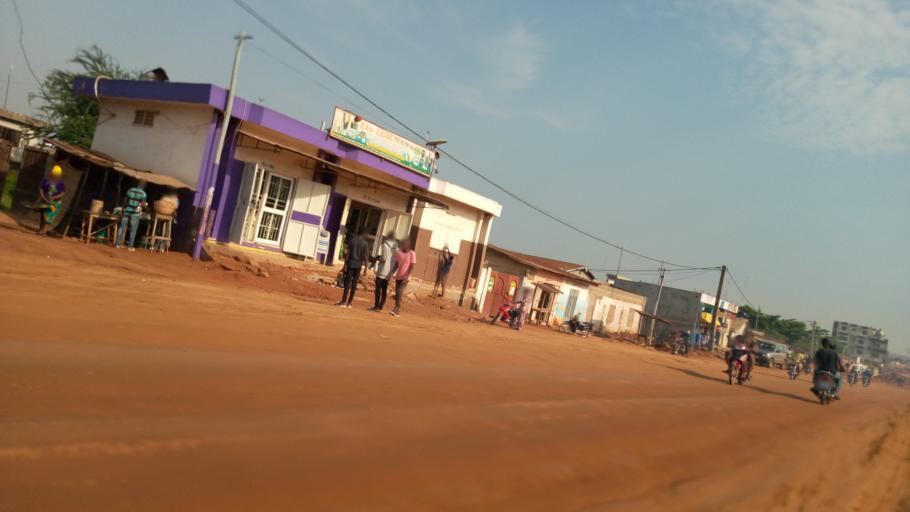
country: BJ
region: Queme
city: Porto-Novo
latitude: 6.4851
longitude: 2.6131
